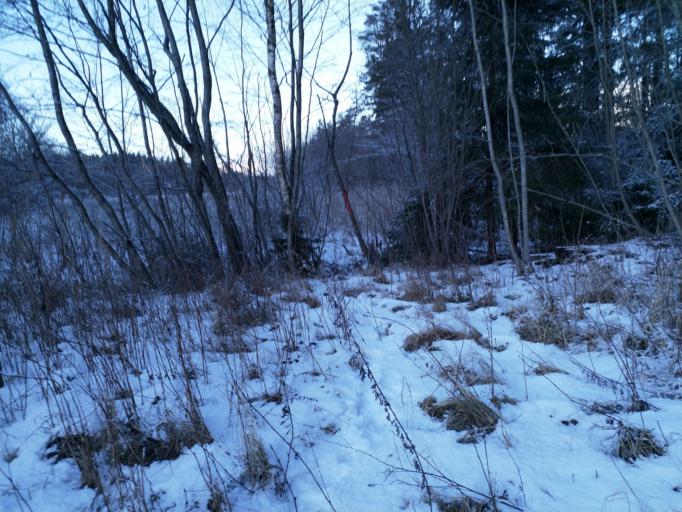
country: LV
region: Skrunda
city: Skrunda
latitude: 56.6787
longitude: 22.0811
